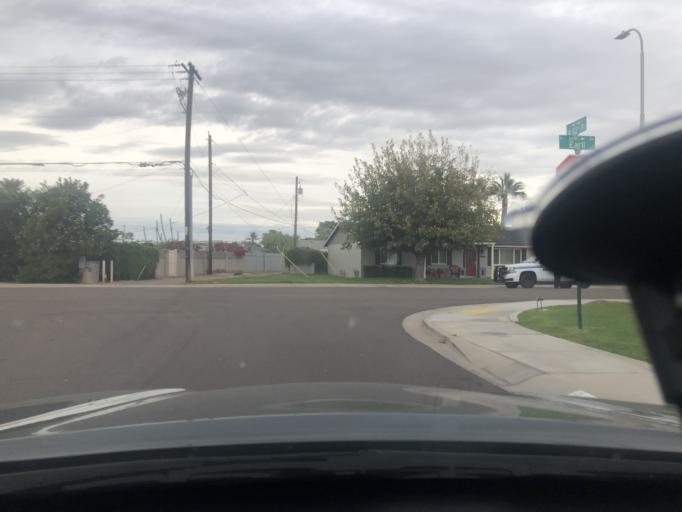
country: US
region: Arizona
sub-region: Maricopa County
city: Scottsdale
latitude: 33.4839
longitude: -111.9019
